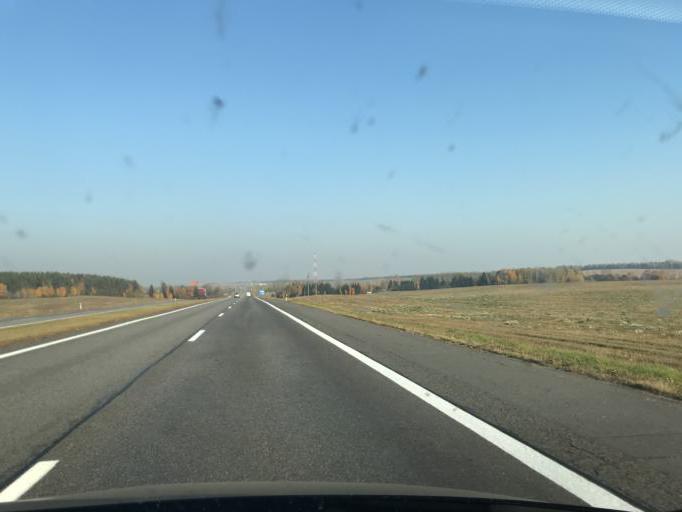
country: BY
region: Minsk
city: Snow
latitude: 53.2910
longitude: 26.3442
